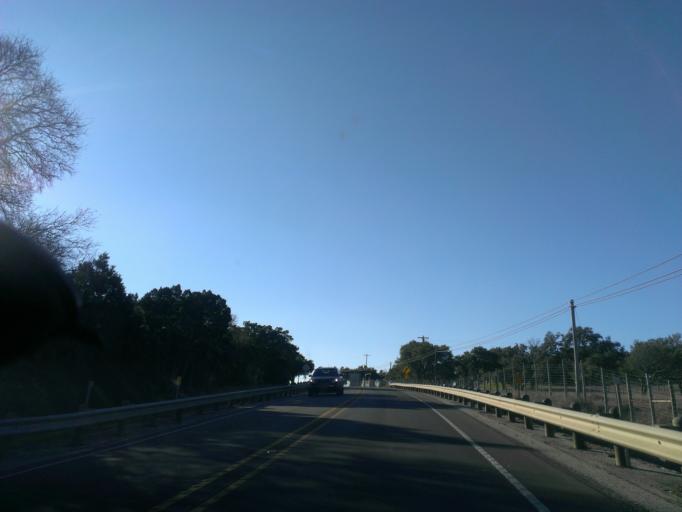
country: US
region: Texas
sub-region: Hays County
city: Dripping Springs
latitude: 30.1574
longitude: -98.0912
